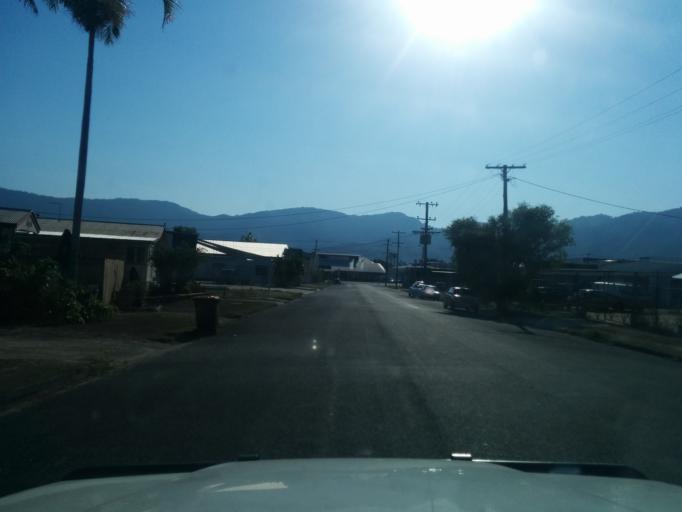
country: AU
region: Queensland
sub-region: Cairns
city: Woree
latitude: -16.9373
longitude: 145.7525
